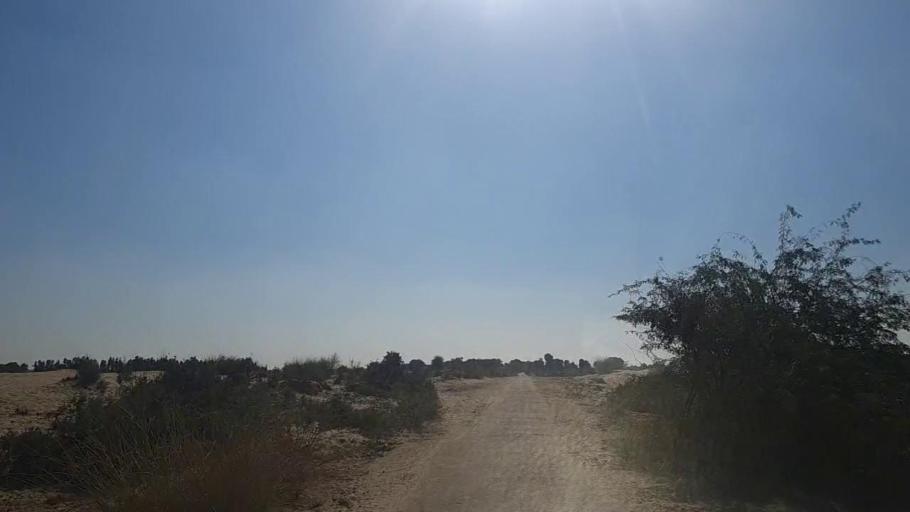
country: PK
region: Sindh
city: Khadro
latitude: 26.1589
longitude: 68.8380
